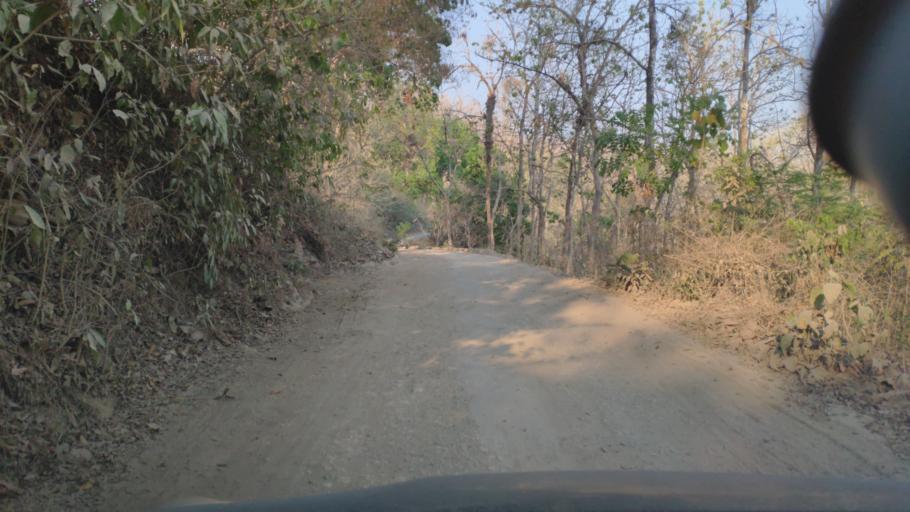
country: ID
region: Central Java
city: Sendangrejo
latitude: -6.9126
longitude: 111.5545
